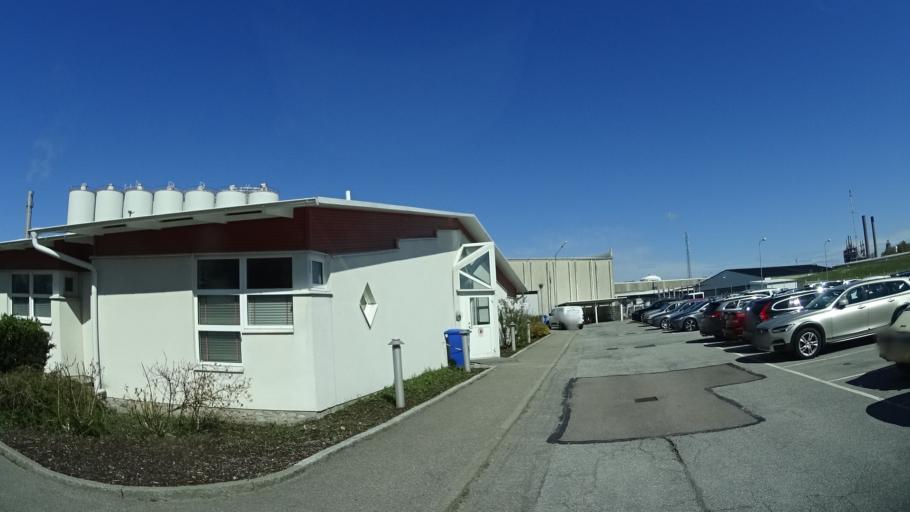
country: SE
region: Vaestra Goetaland
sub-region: Stenungsunds Kommun
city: Stenungsund
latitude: 58.0797
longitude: 11.8149
